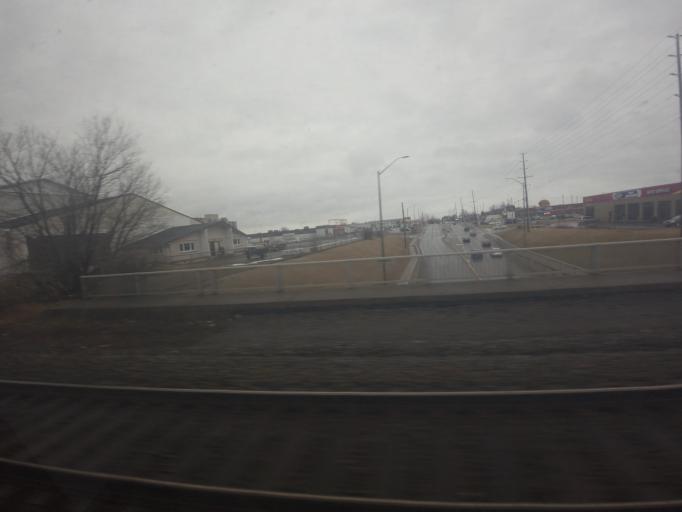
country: CA
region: Ontario
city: Kingston
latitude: 44.2407
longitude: -76.5679
